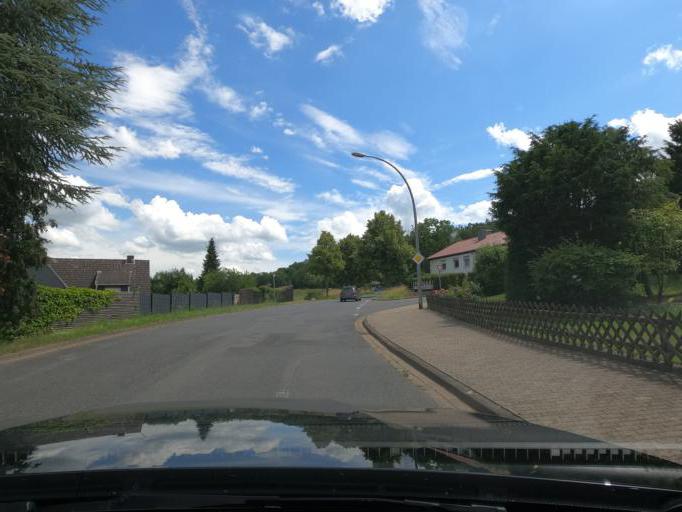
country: DE
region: Lower Saxony
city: Elbe
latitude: 52.1246
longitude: 10.2919
